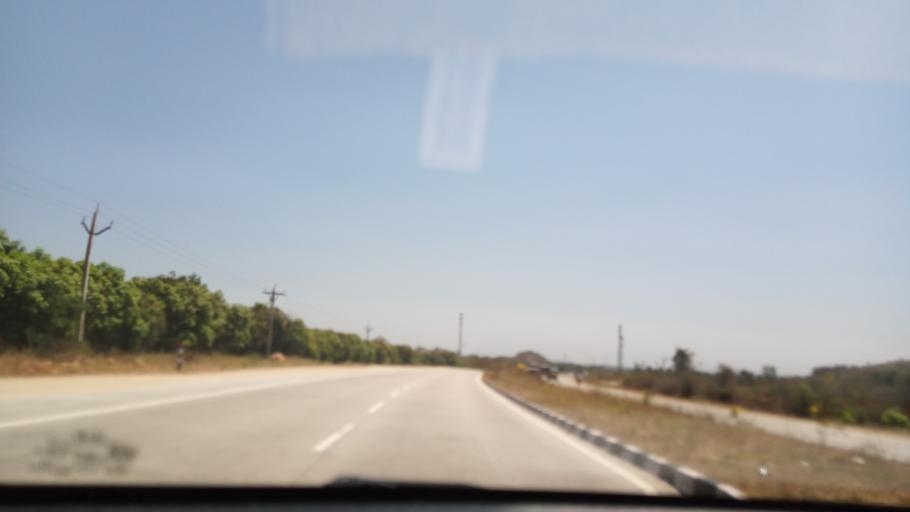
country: IN
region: Andhra Pradesh
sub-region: Chittoor
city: Chittoor
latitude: 13.2014
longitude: 78.9631
